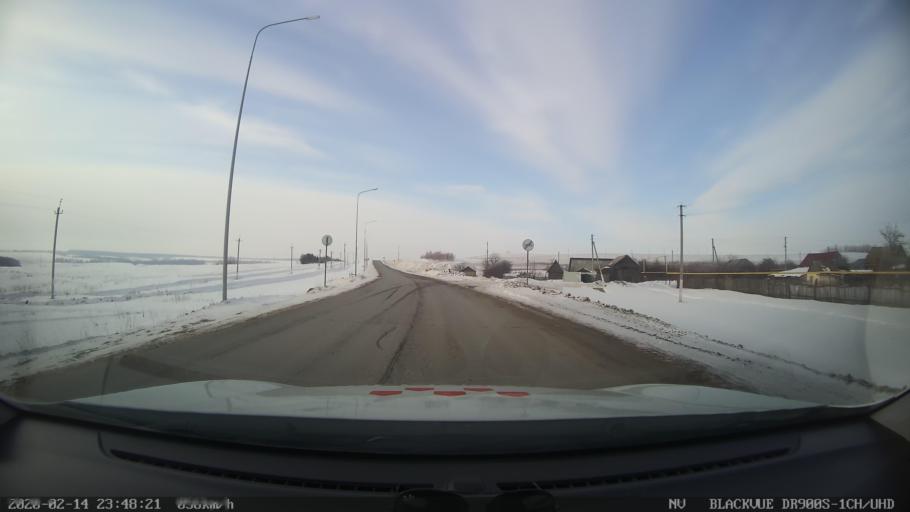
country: RU
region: Tatarstan
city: Kuybyshevskiy Zaton
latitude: 55.2475
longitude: 49.2037
